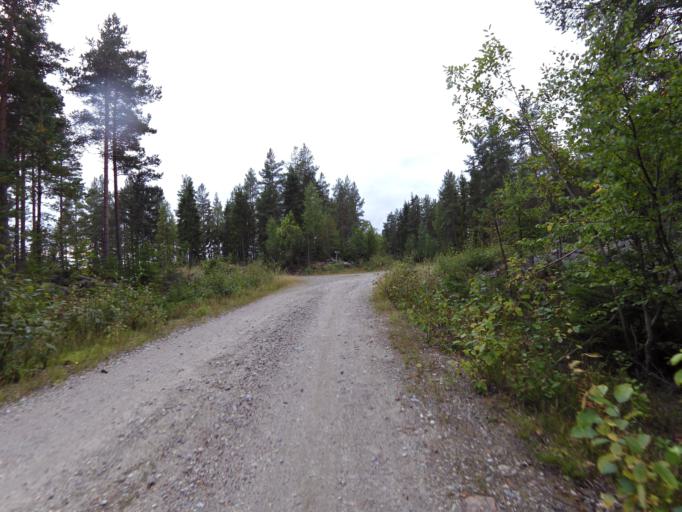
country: SE
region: Gaevleborg
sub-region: Gavle Kommun
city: Valbo
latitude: 60.7445
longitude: 16.9836
